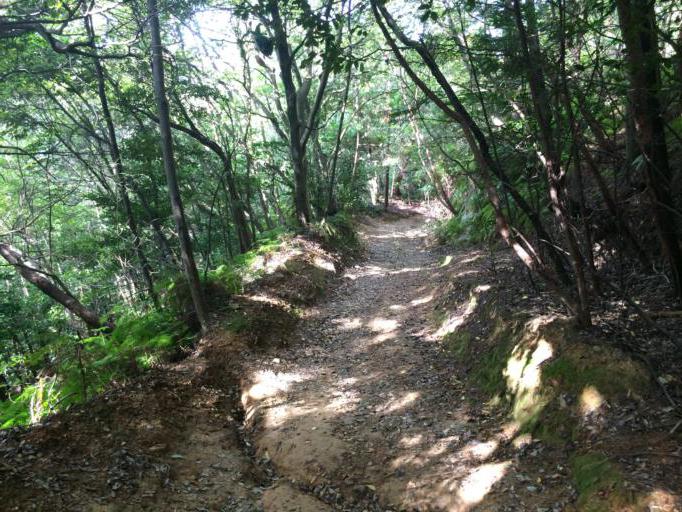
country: JP
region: Kyoto
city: Uji
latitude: 34.9504
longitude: 135.8292
